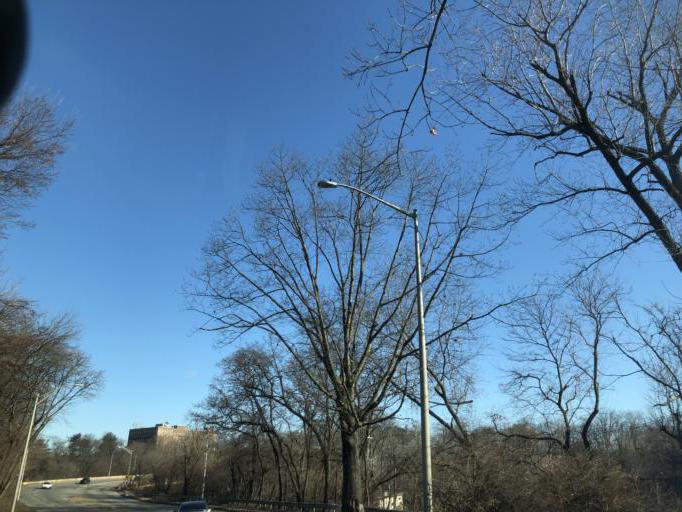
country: US
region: Pennsylvania
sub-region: Delaware County
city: Millbourne
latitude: 39.9557
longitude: -75.2513
